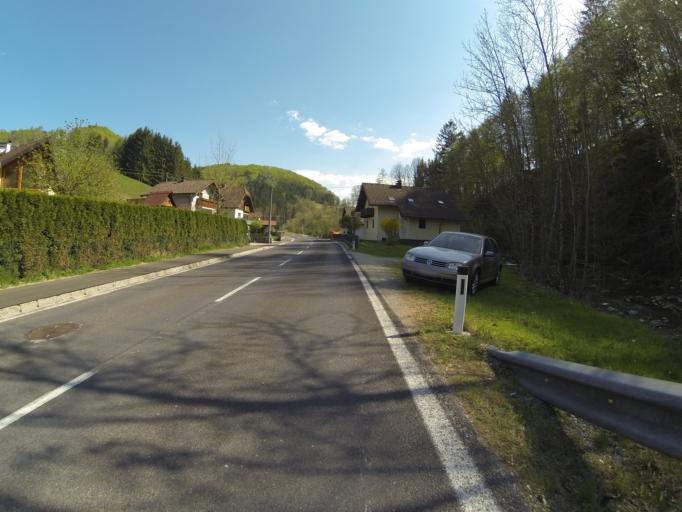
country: AT
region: Upper Austria
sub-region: Politischer Bezirk Gmunden
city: Altmunster
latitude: 47.9049
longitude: 13.7094
